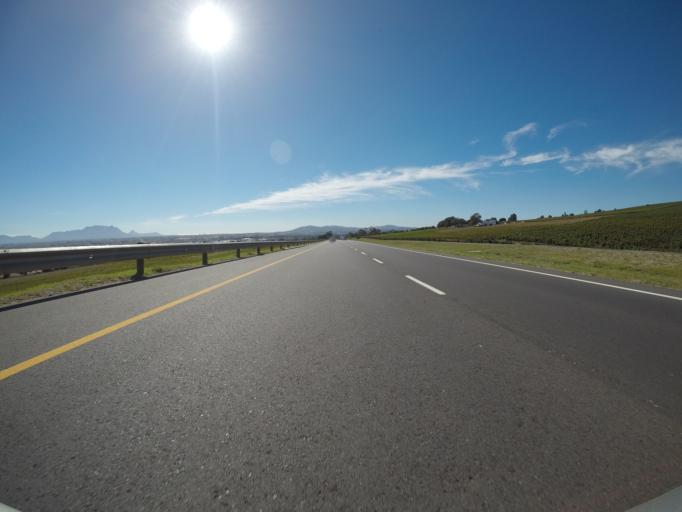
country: ZA
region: Western Cape
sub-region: City of Cape Town
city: Kraaifontein
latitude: -33.9615
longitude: 18.7280
